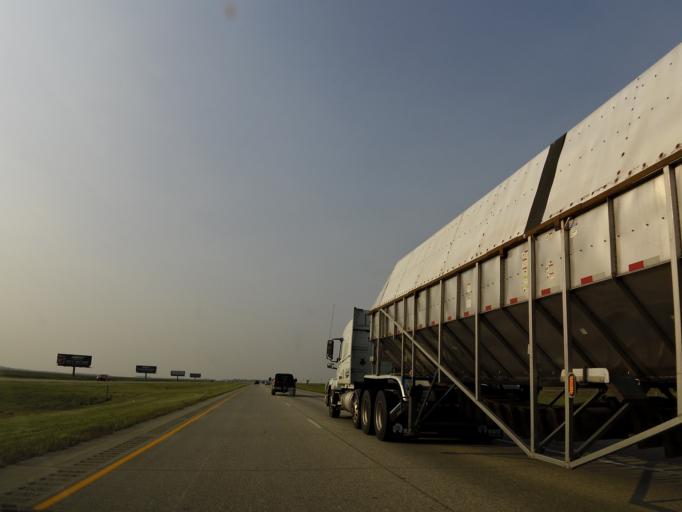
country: US
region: North Dakota
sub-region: Cass County
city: West Fargo
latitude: 47.0204
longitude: -96.9111
